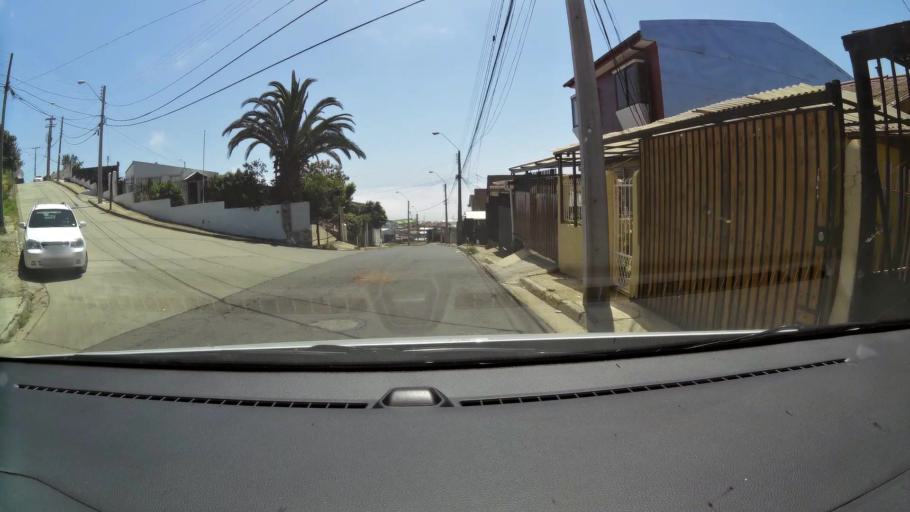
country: CL
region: Valparaiso
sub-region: Provincia de Valparaiso
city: Valparaiso
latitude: -33.0410
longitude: -71.6443
